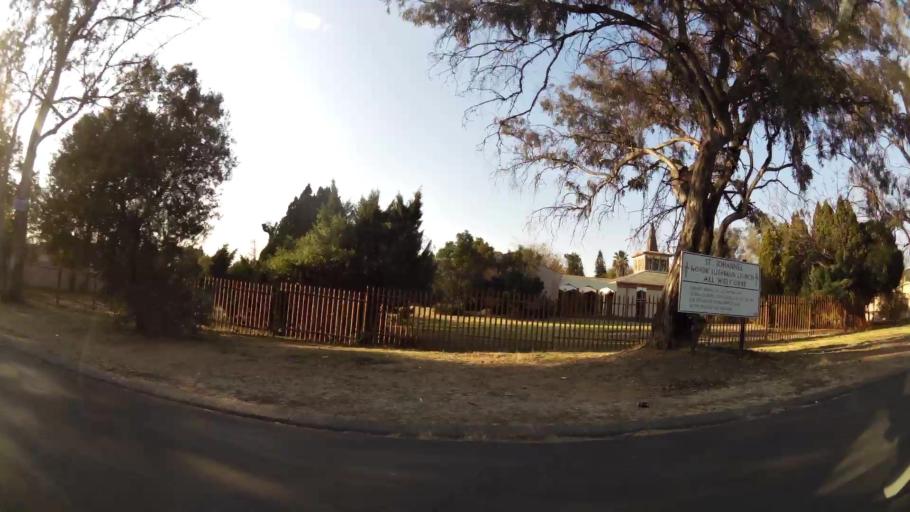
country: ZA
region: Gauteng
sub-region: City of Johannesburg Metropolitan Municipality
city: Modderfontein
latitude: -26.0758
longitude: 28.0917
